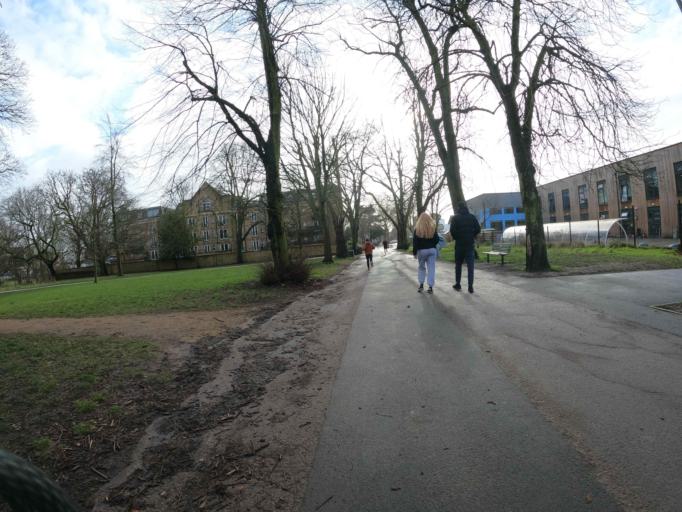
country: GB
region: England
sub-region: Greater London
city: Acton
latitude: 51.5075
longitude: -0.2623
